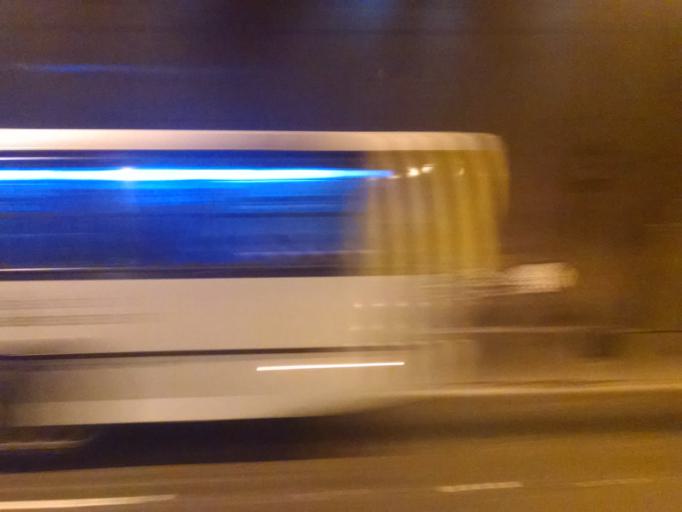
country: BR
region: Rio de Janeiro
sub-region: Rio De Janeiro
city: Rio de Janeiro
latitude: -22.9811
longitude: -43.2329
